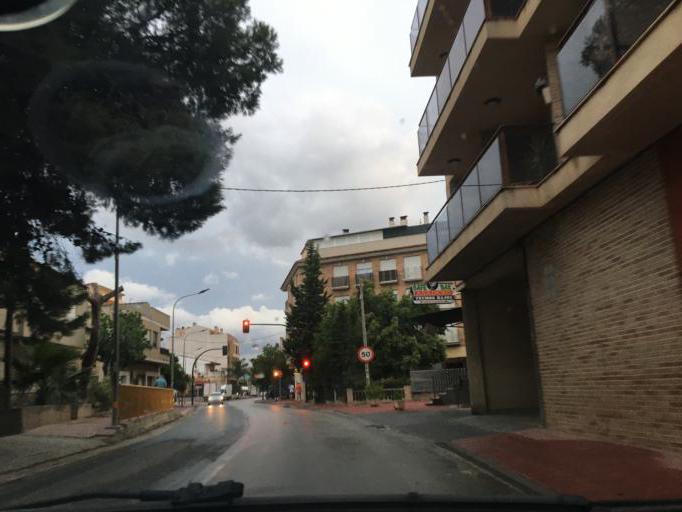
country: ES
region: Murcia
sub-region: Murcia
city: Santomera
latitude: 38.0161
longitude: -1.0528
